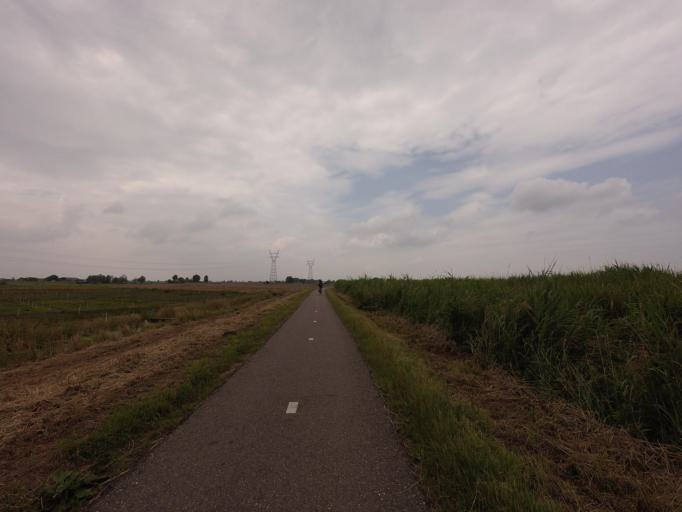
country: NL
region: North Holland
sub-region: Gemeente Purmerend
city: Purmerend
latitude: 52.4734
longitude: 4.9558
